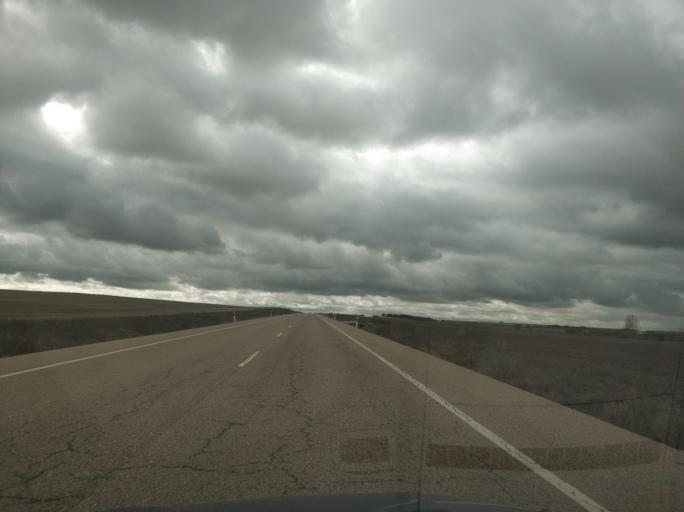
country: ES
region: Castille and Leon
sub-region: Provincia de Valladolid
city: Alaejos
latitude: 41.2790
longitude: -5.2489
